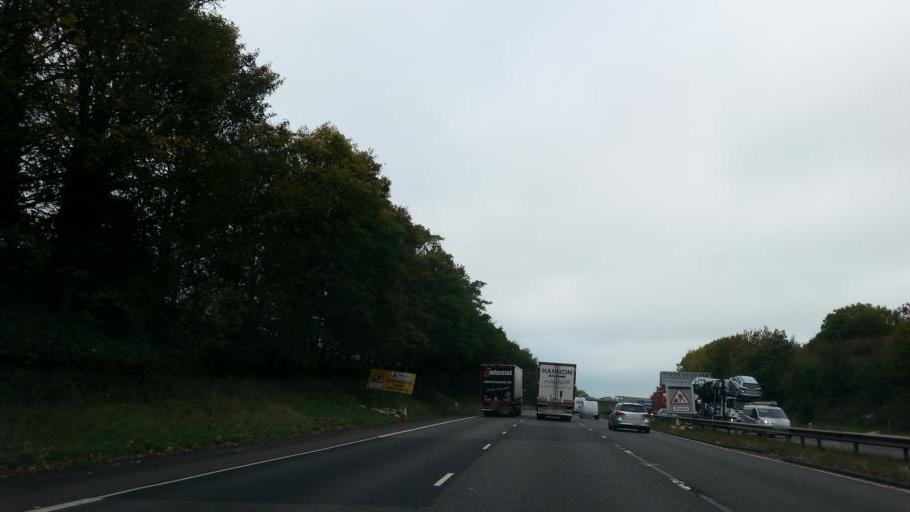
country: GB
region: England
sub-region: Staffordshire
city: Stafford
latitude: 52.7868
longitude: -2.1368
